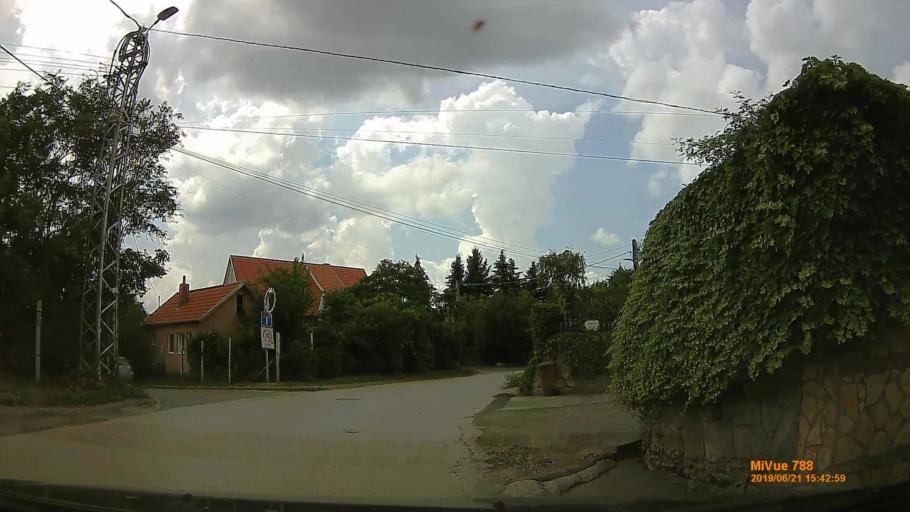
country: HU
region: Baranya
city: Pecs
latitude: 46.0833
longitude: 18.2025
